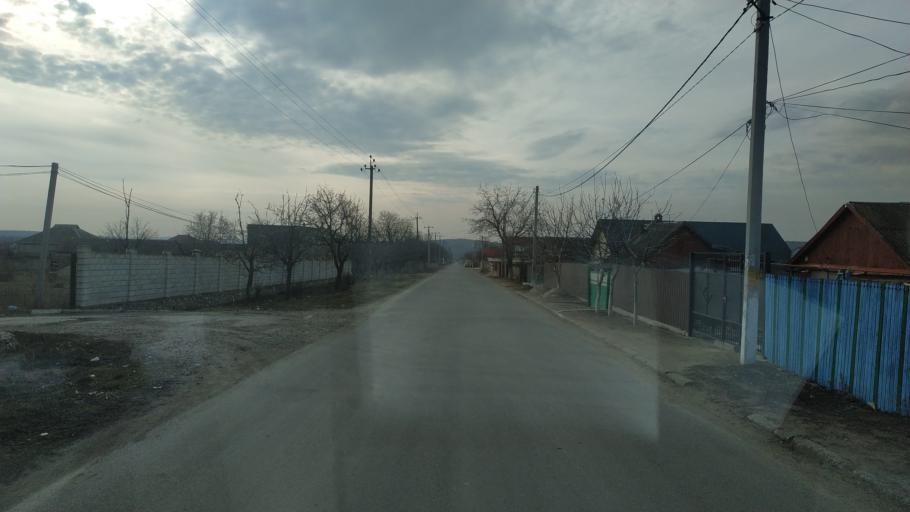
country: MD
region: Chisinau
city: Singera
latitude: 46.9673
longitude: 29.0651
